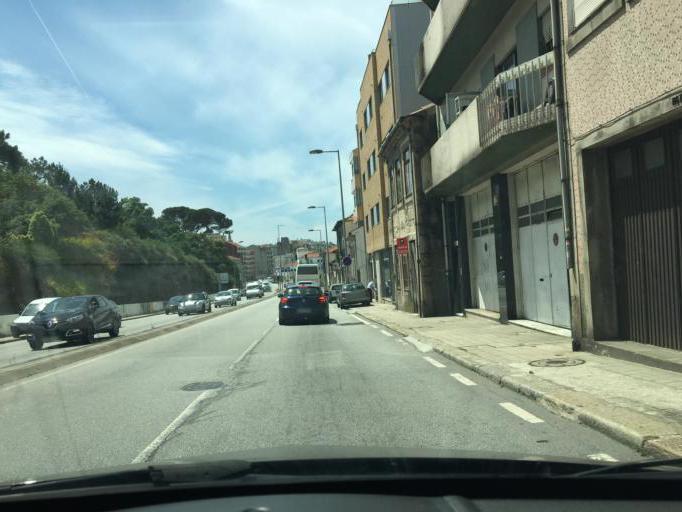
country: PT
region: Porto
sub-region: Porto
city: Porto
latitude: 41.1676
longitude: -8.6065
